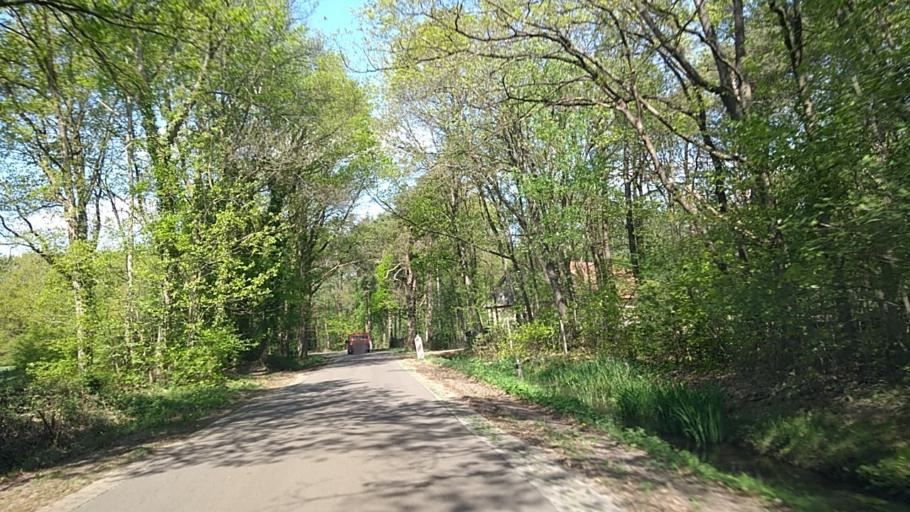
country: NL
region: Overijssel
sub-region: Gemeente Haaksbergen
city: Haaksbergen
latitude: 52.1334
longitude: 6.7284
